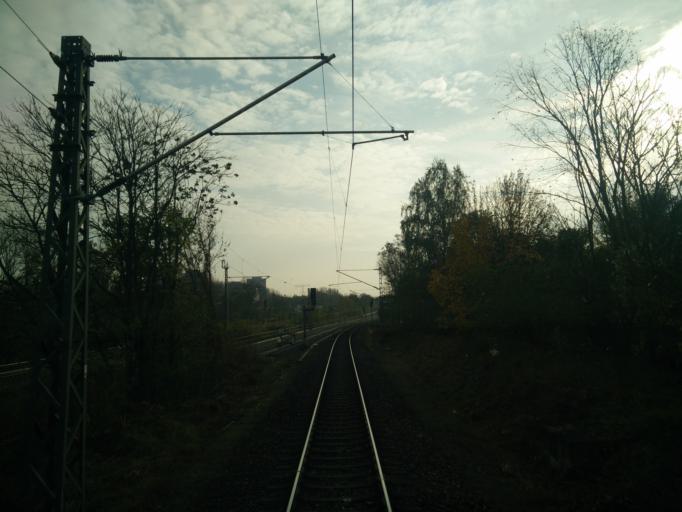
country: DE
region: Berlin
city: Rummelsburg
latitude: 52.4964
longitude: 13.4900
